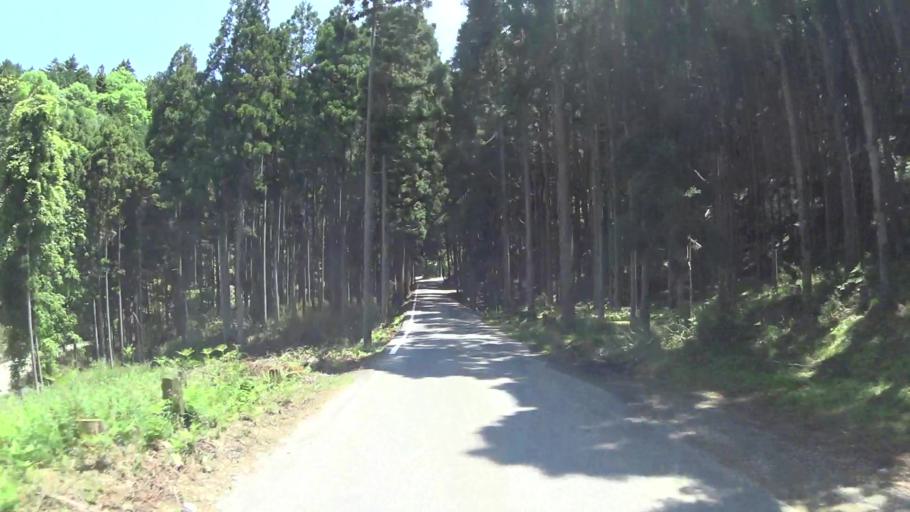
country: JP
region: Kyoto
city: Kameoka
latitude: 35.1370
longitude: 135.5859
